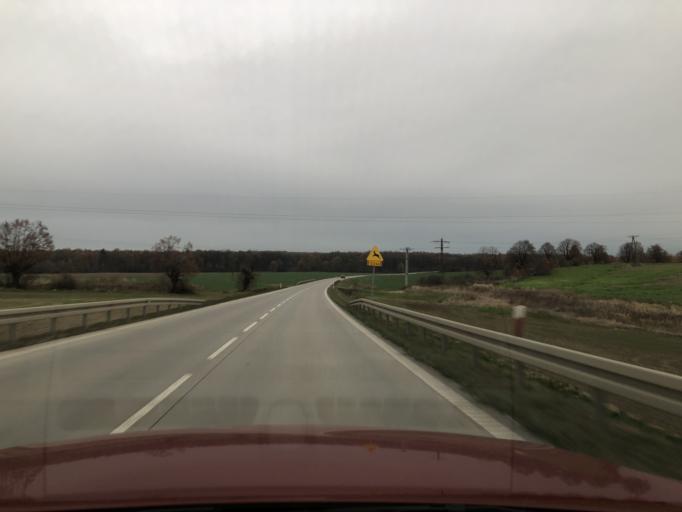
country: PL
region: Lower Silesian Voivodeship
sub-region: Powiat swidnicki
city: Zarow
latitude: 50.9378
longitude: 16.4729
